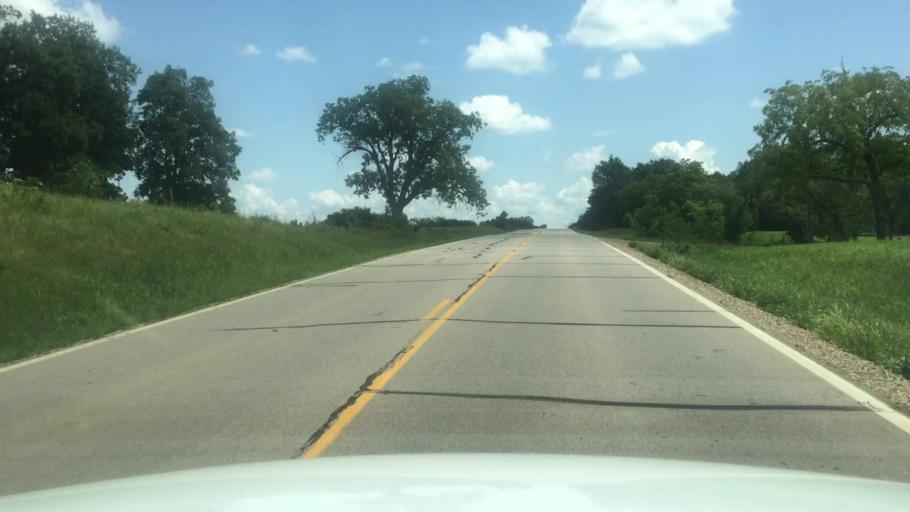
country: US
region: Kansas
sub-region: Brown County
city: Horton
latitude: 39.6674
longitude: -95.6334
